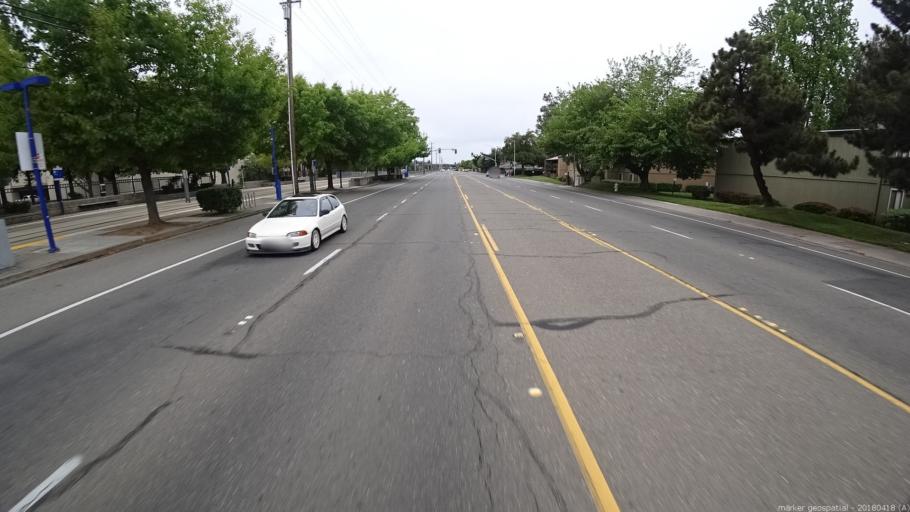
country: US
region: California
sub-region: Sacramento County
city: La Riviera
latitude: 38.5643
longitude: -121.3528
